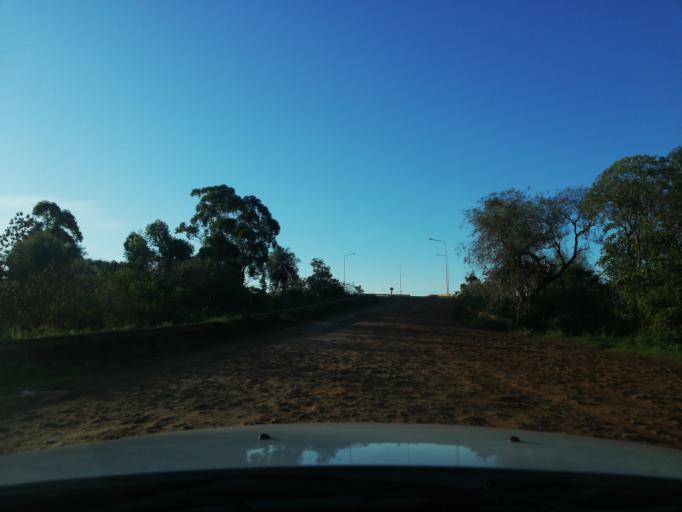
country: AR
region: Misiones
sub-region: Departamento de Capital
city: Posadas
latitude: -27.4671
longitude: -55.9709
